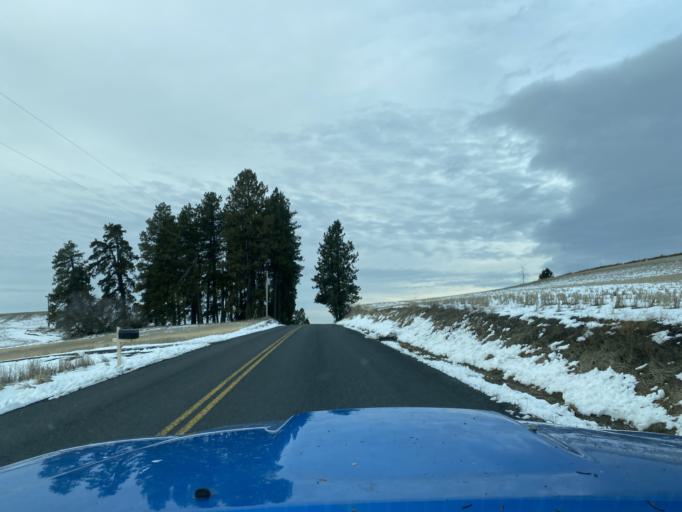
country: US
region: Idaho
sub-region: Latah County
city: Moscow
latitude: 46.7001
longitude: -116.9314
